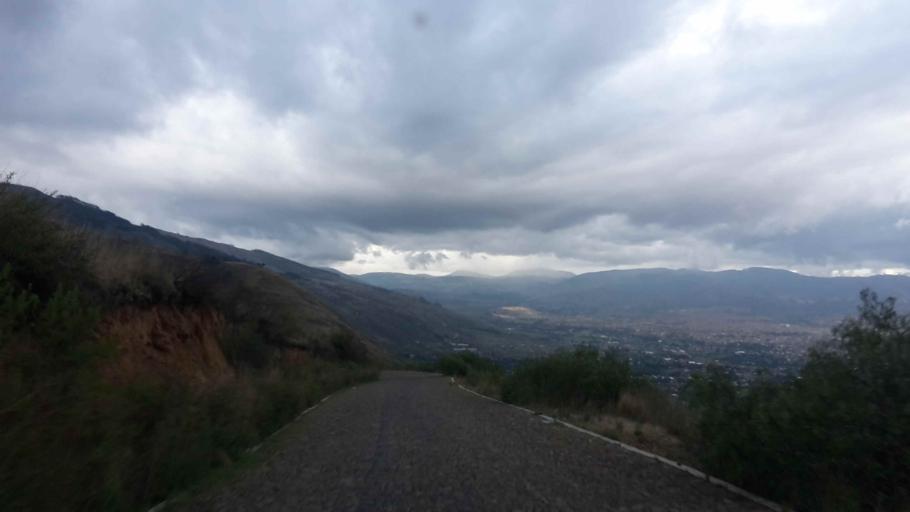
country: BO
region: Cochabamba
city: Cochabamba
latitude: -17.3664
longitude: -66.0648
